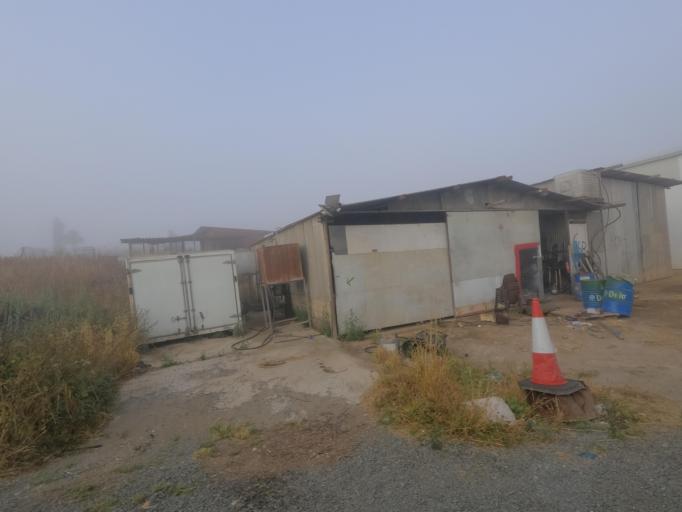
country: CY
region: Ammochostos
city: Acheritou
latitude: 35.0853
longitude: 33.8763
